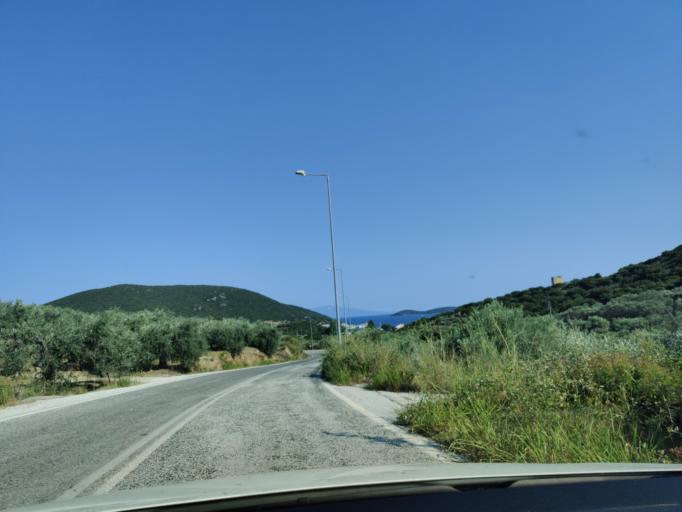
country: GR
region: East Macedonia and Thrace
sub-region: Nomos Kavalas
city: Nea Iraklitsa
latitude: 40.8572
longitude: 24.3092
